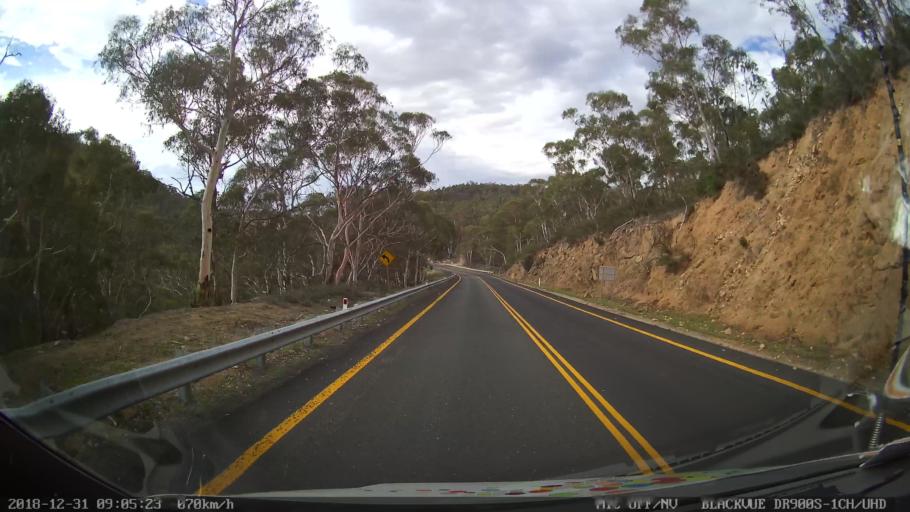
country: AU
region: New South Wales
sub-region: Snowy River
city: Jindabyne
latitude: -36.3626
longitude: 148.5869
